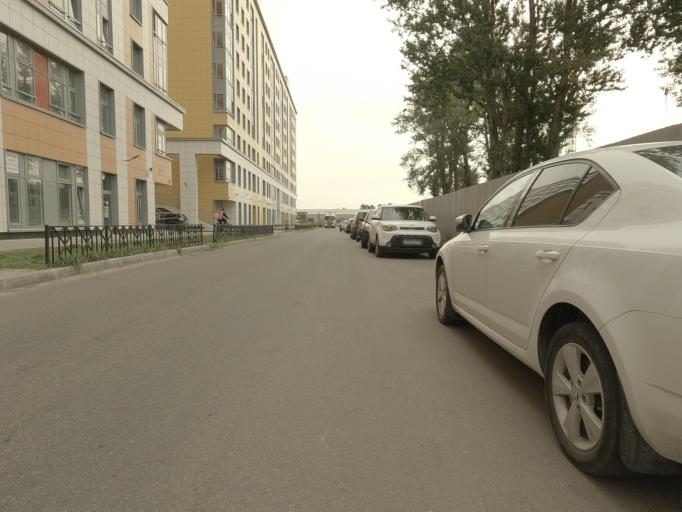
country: RU
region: St.-Petersburg
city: Admiralteisky
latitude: 59.8976
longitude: 30.3071
